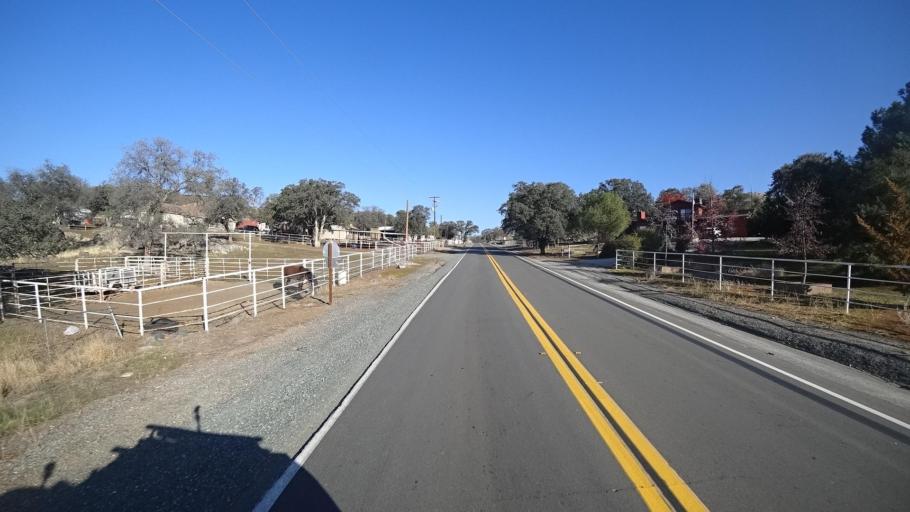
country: US
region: California
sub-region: Tulare County
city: Richgrove
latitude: 35.7044
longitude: -118.8364
